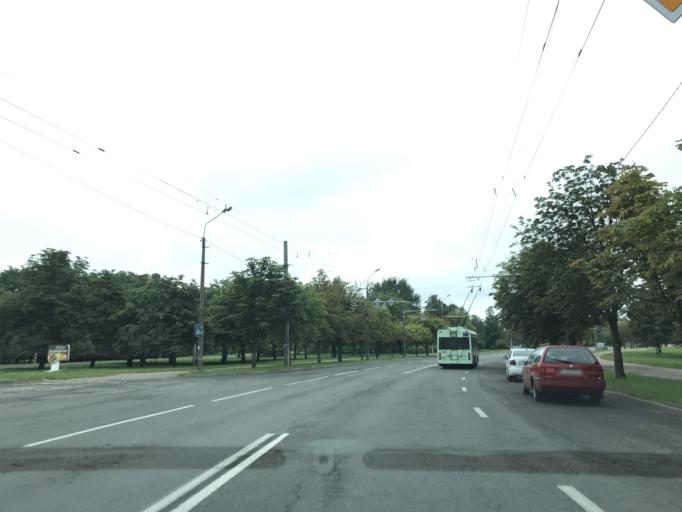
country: BY
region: Minsk
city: Borovlyany
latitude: 53.9494
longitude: 27.6406
